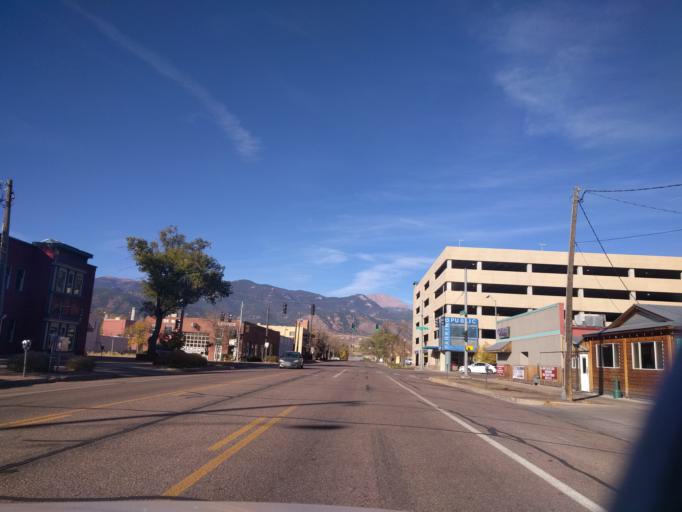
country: US
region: Colorado
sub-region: El Paso County
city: Colorado Springs
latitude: 38.8283
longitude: -104.8229
